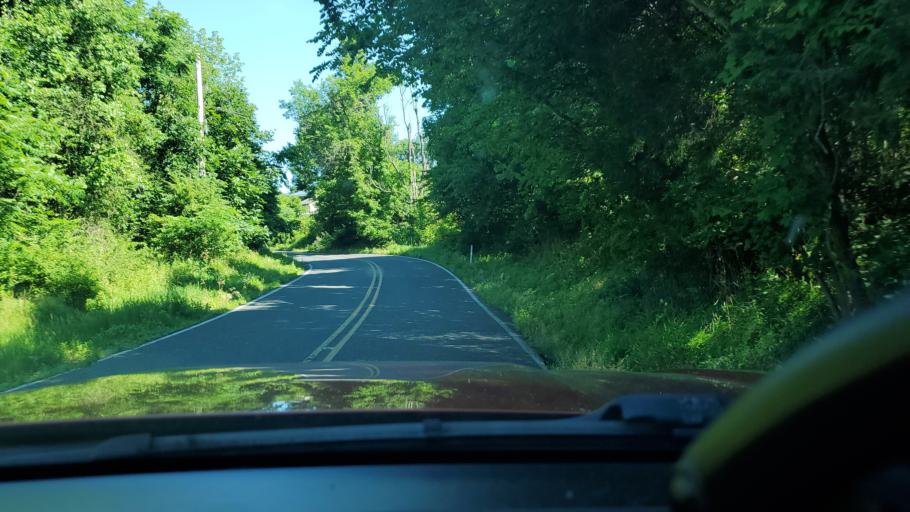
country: US
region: Pennsylvania
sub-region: Montgomery County
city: Pennsburg
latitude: 40.3721
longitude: -75.5120
